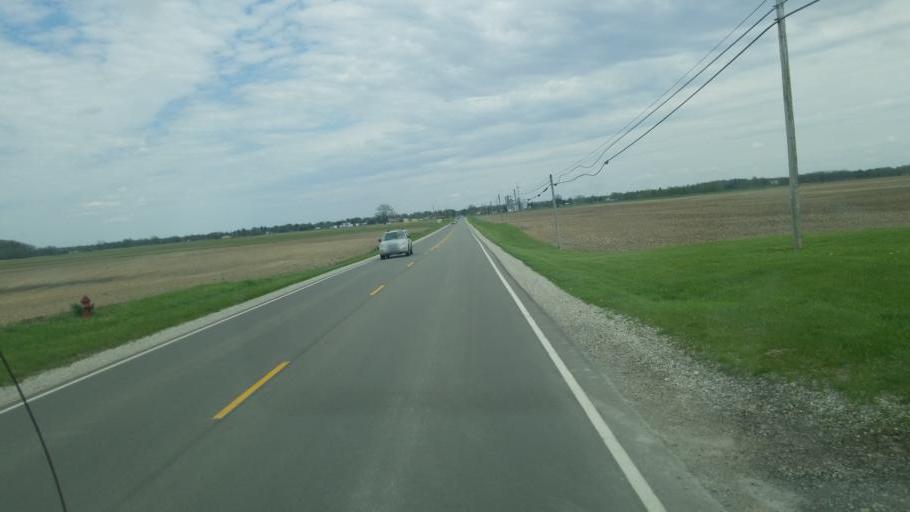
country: US
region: Ohio
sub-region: Crawford County
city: Bucyrus
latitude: 40.8177
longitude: -83.0116
